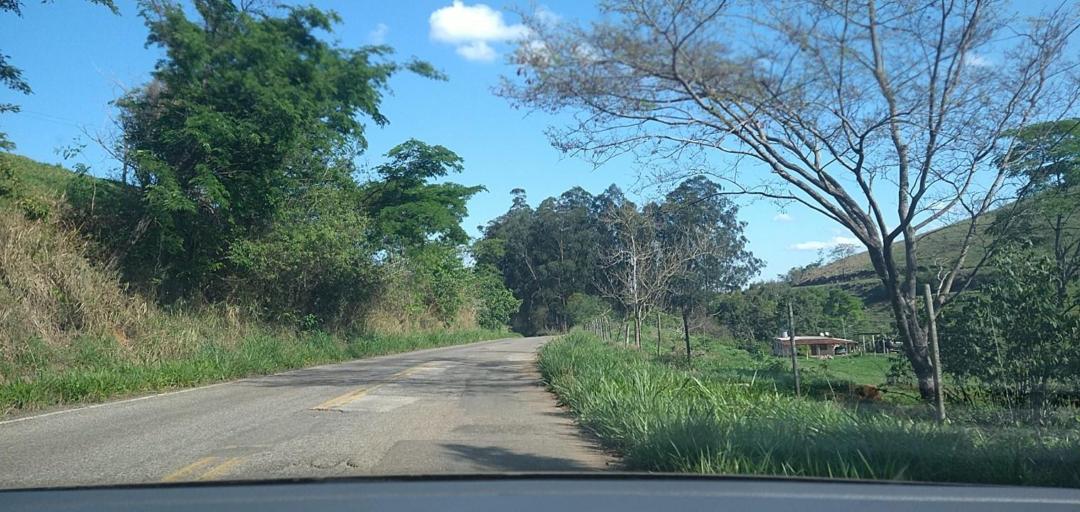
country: BR
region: Minas Gerais
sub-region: Alvinopolis
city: Alvinopolis
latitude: -20.1949
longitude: -42.9318
